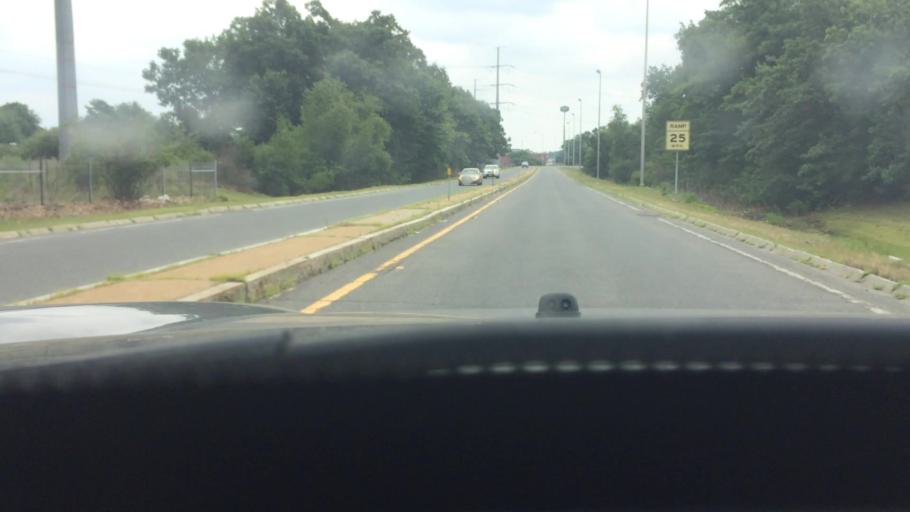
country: US
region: Massachusetts
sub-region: Hampden County
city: North Chicopee
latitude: 42.1729
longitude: -72.5856
